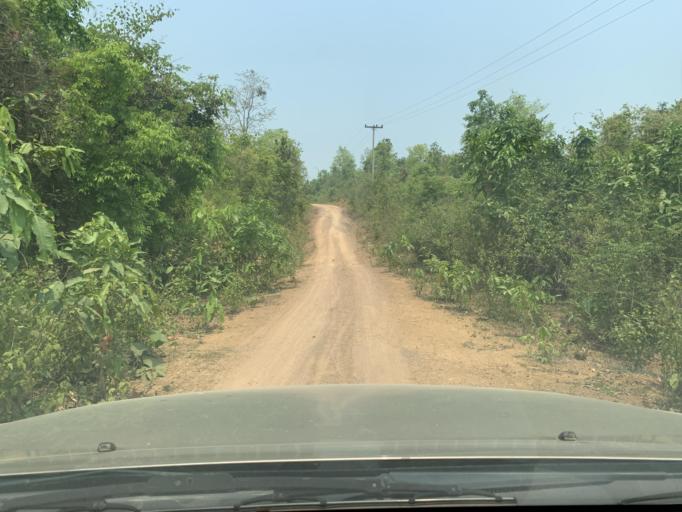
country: LA
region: Louangphabang
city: Louangphabang
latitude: 19.9564
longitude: 102.1279
